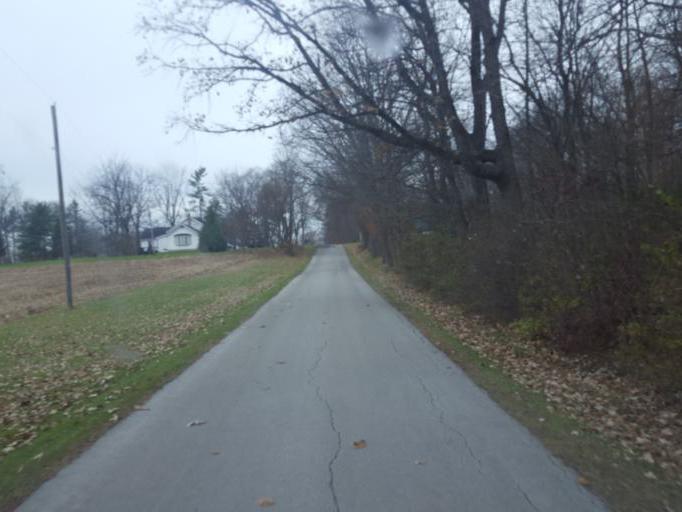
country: US
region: Ohio
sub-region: Morrow County
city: Cardington
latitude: 40.5312
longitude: -82.8671
